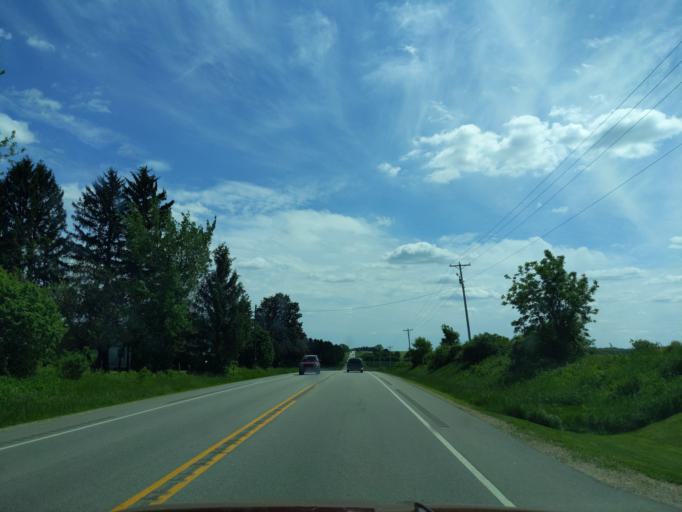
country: US
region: Wisconsin
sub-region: Columbia County
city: Poynette
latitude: 43.3785
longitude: -89.3282
